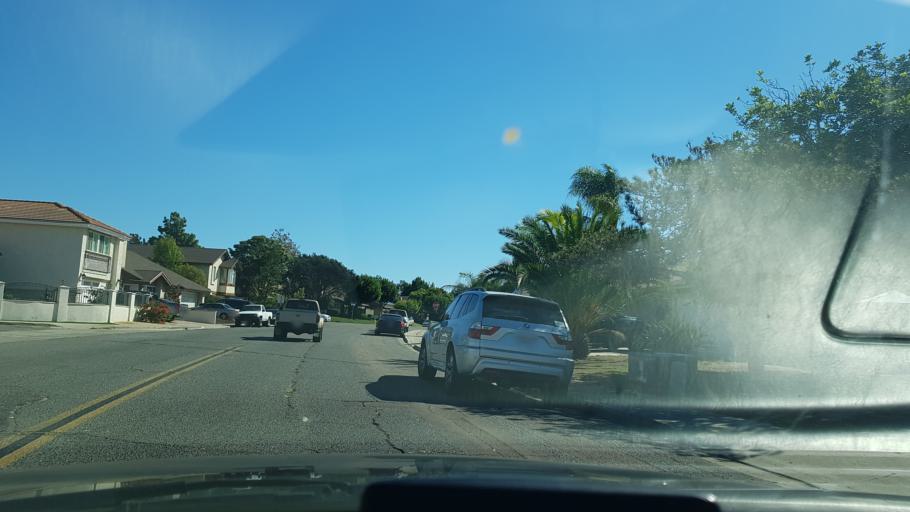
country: US
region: California
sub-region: San Diego County
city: Fairbanks Ranch
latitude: 32.9129
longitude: -117.1319
